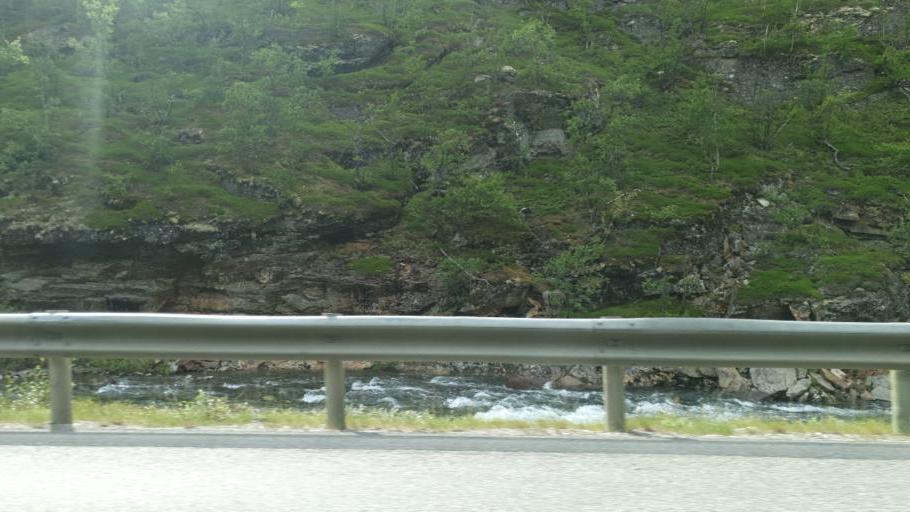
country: NO
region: Sor-Trondelag
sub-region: Oppdal
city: Oppdal
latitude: 62.3538
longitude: 9.6321
